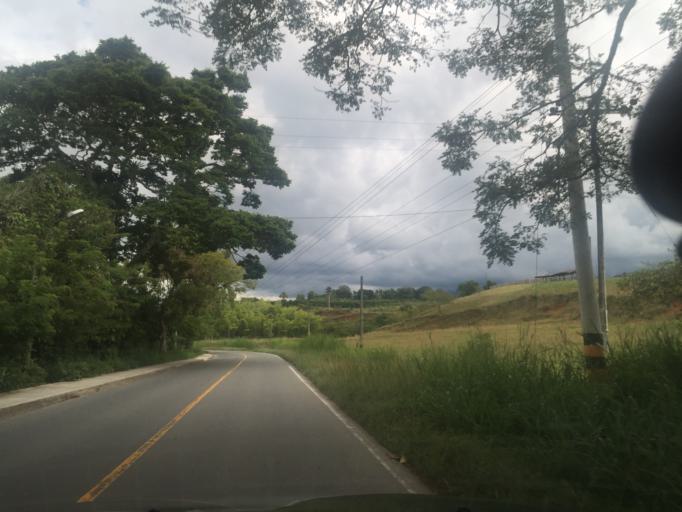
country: CO
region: Valle del Cauca
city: Caicedonia
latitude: 4.3410
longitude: -75.8469
